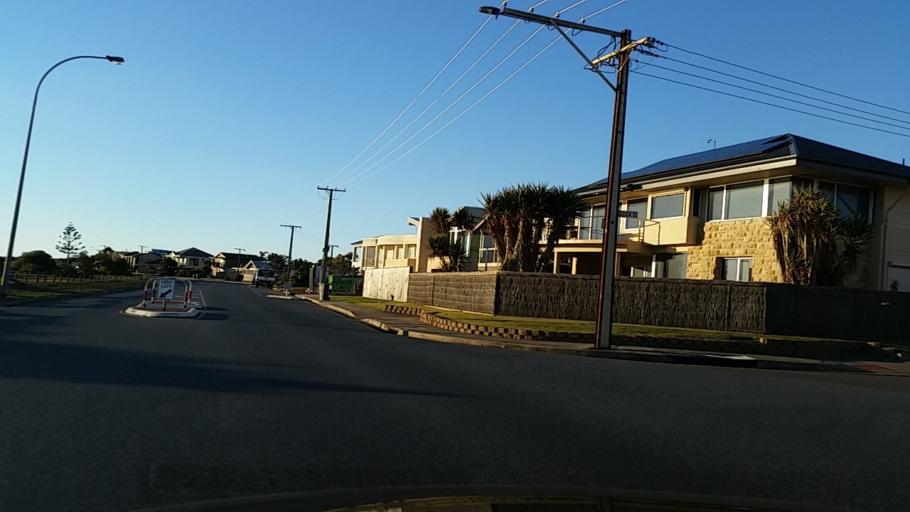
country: AU
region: South Australia
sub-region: Onkaparinga
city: Seaford
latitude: -35.1766
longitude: 138.4672
